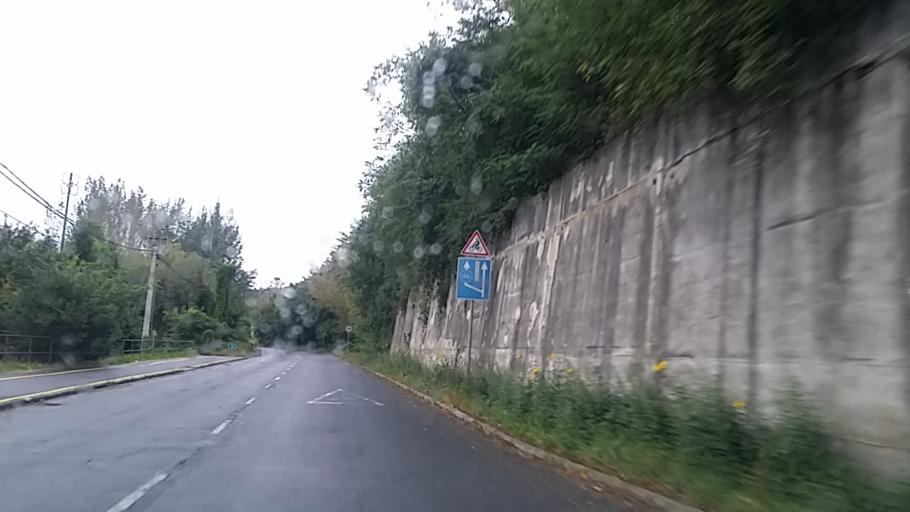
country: HU
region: Komarom-Esztergom
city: Pilismarot
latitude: 47.7939
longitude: 18.9110
